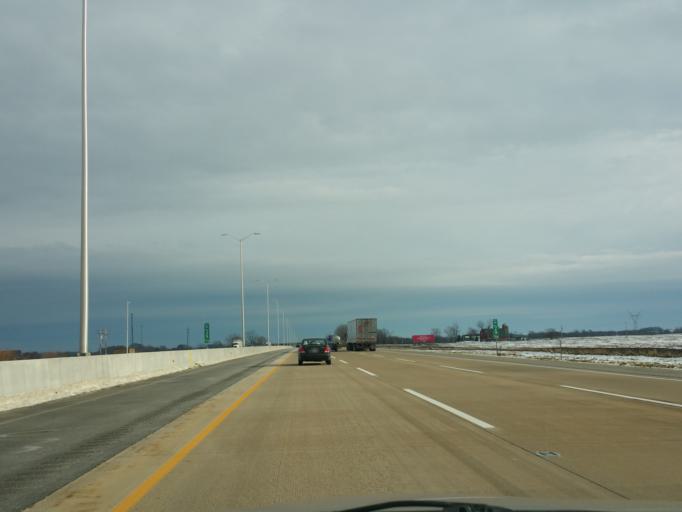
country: US
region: Illinois
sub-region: DeKalb County
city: Kingston
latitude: 42.2145
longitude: -88.7328
